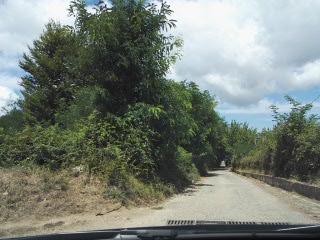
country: IT
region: Calabria
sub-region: Provincia di Vibo-Valentia
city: Serra San Bruno
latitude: 38.5593
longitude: 16.3315
